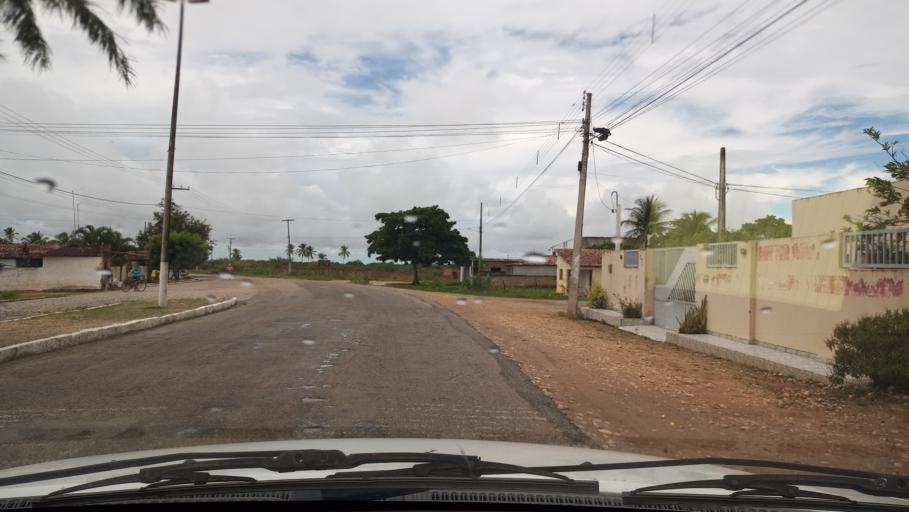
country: BR
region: Rio Grande do Norte
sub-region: Poco Branco
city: Poco Branco
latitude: -5.6184
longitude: -35.6554
